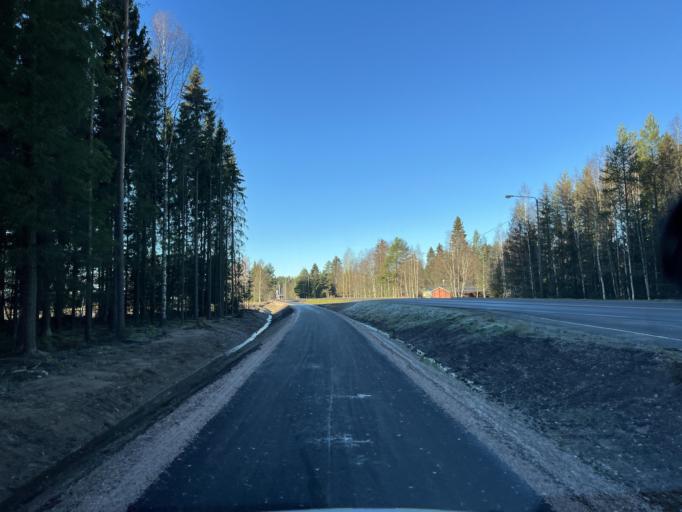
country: FI
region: Northern Ostrobothnia
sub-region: Nivala-Haapajaervi
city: Nivala
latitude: 63.9502
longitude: 24.9174
